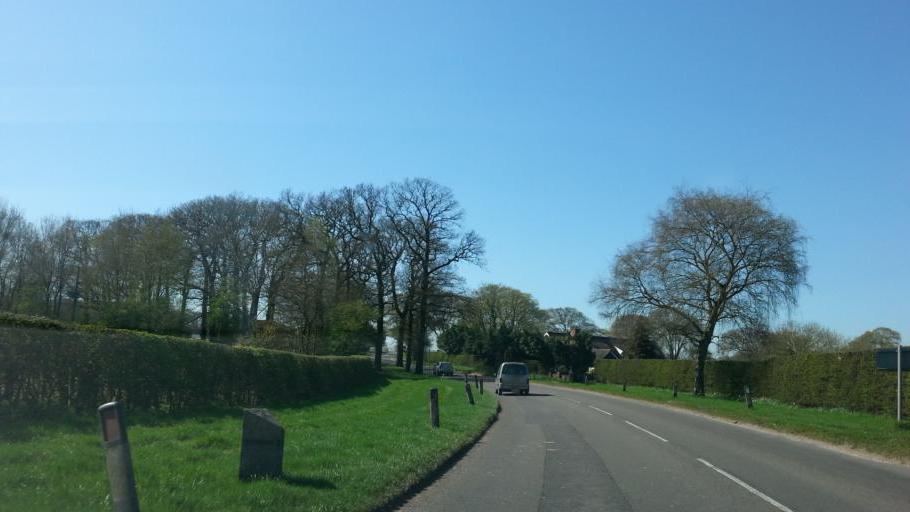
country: GB
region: England
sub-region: Staffordshire
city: Stafford
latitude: 52.8290
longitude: -2.0649
